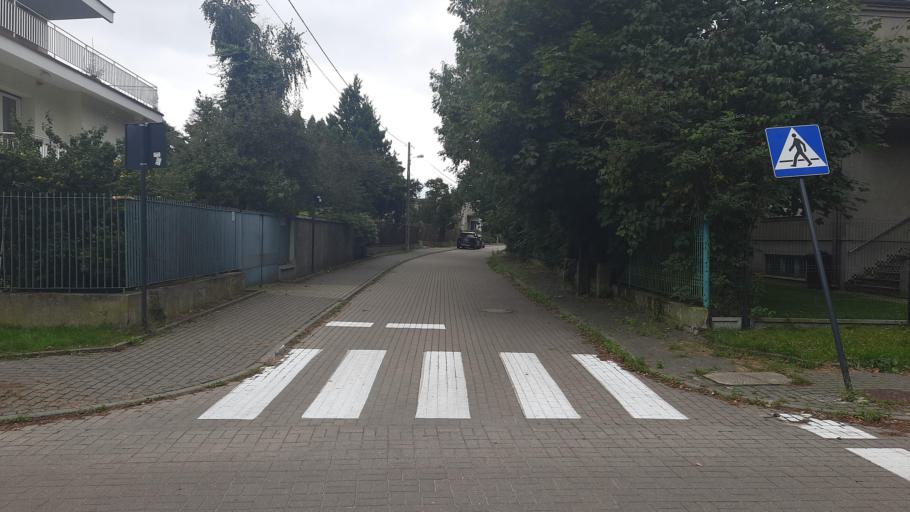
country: PL
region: Lodz Voivodeship
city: Lodz
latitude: 51.8050
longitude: 19.4506
